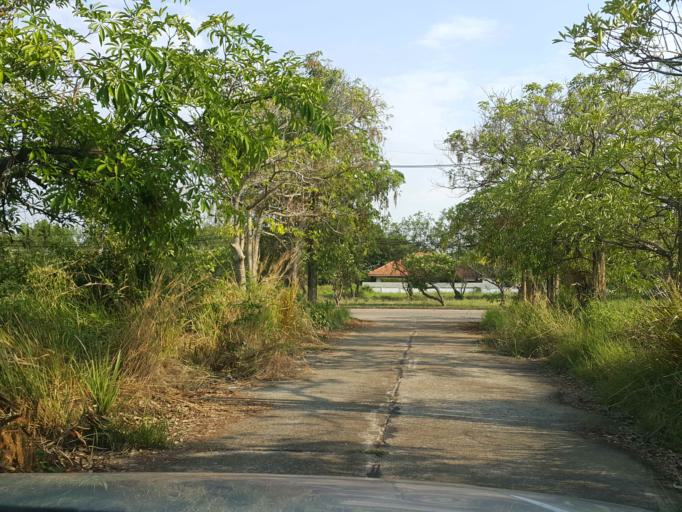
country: TH
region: Chiang Mai
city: Hang Dong
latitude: 18.6978
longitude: 98.9379
